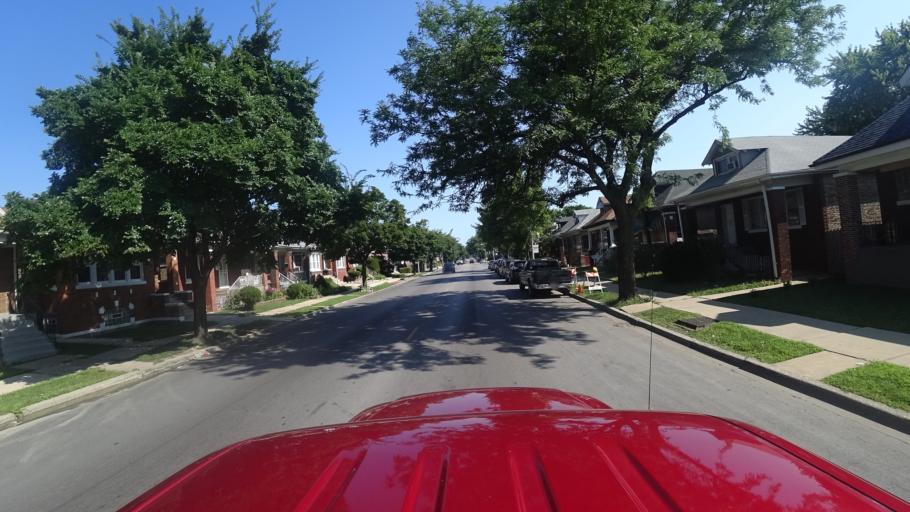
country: US
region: Illinois
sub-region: Cook County
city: Hometown
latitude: 41.7909
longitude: -87.6937
